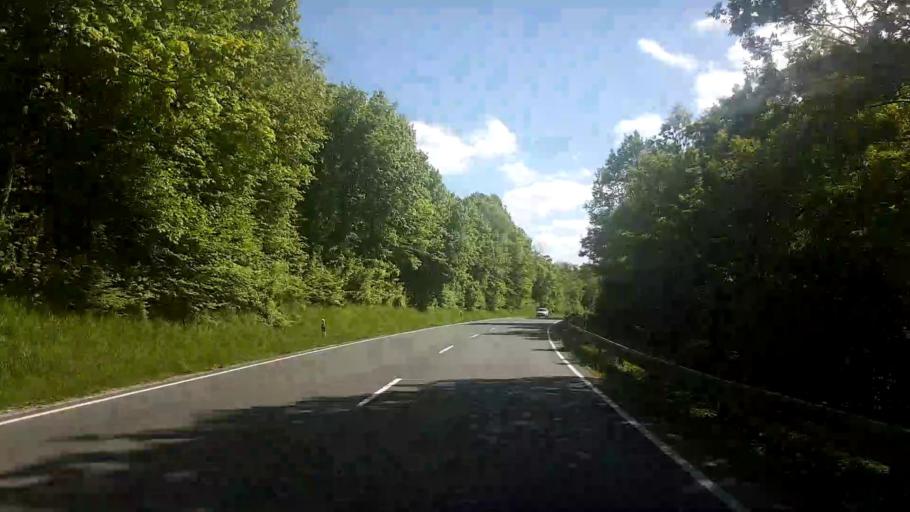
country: DE
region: Bavaria
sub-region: Upper Franconia
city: Rattelsdorf
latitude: 50.0581
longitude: 10.8782
